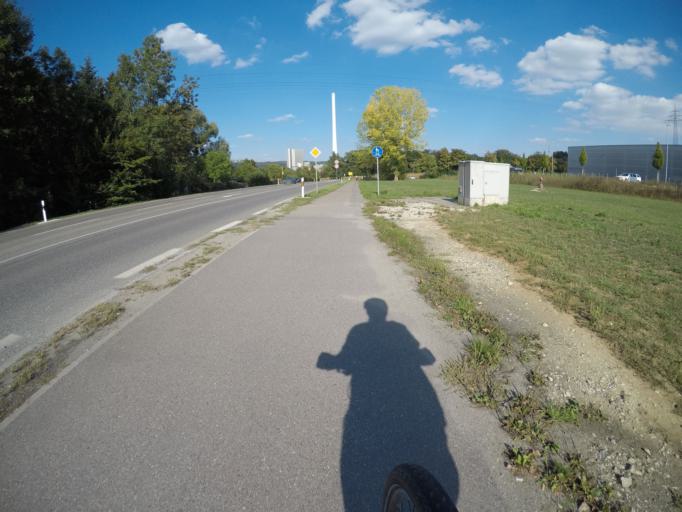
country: DE
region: Baden-Wuerttemberg
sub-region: Regierungsbezirk Stuttgart
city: Altbach
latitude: 48.7119
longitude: 9.3584
